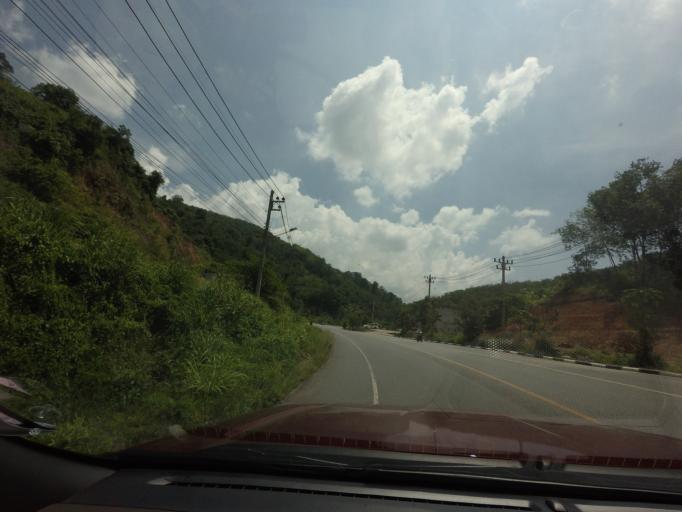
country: TH
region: Yala
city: Betong
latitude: 5.7911
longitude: 101.0723
